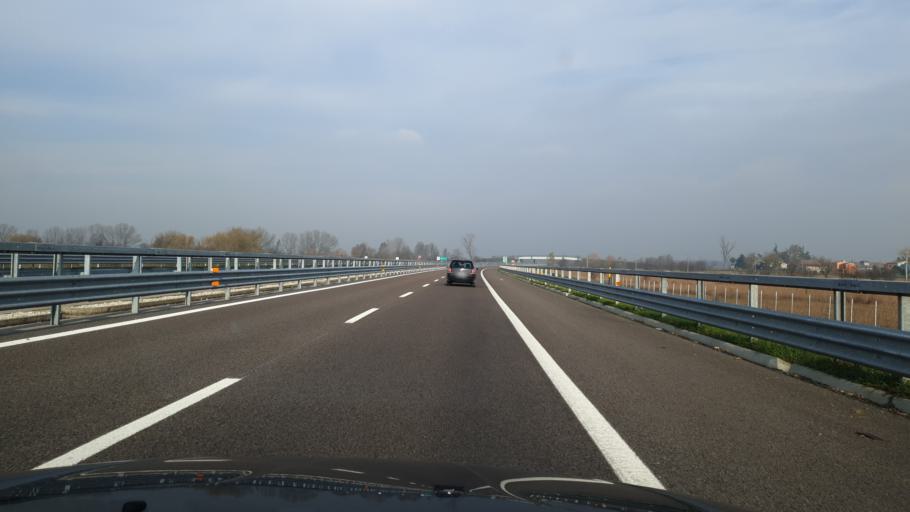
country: IT
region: Veneto
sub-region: Provincia di Padova
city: Megliadino San Vitale
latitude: 45.1710
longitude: 11.5344
